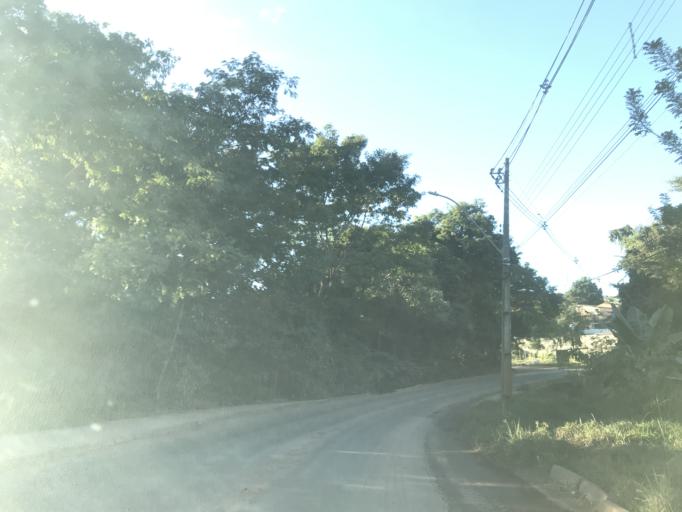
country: BR
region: Federal District
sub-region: Brasilia
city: Brasilia
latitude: -15.8820
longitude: -47.7804
